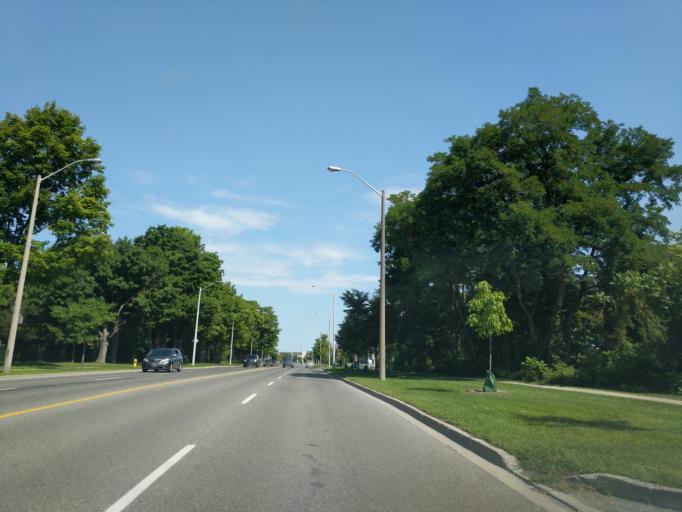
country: CA
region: Ontario
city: Scarborough
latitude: 43.8135
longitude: -79.2262
